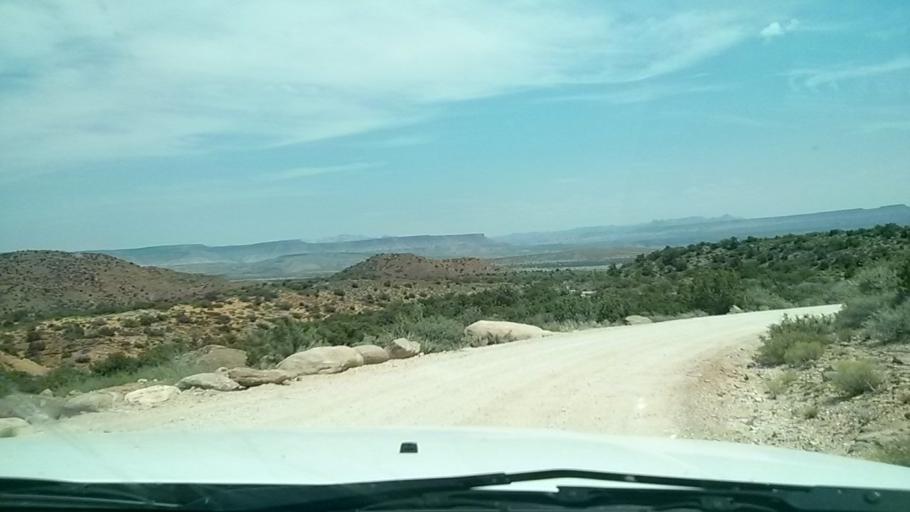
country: US
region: Utah
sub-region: Washington County
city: Toquerville
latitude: 37.2698
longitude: -113.3761
